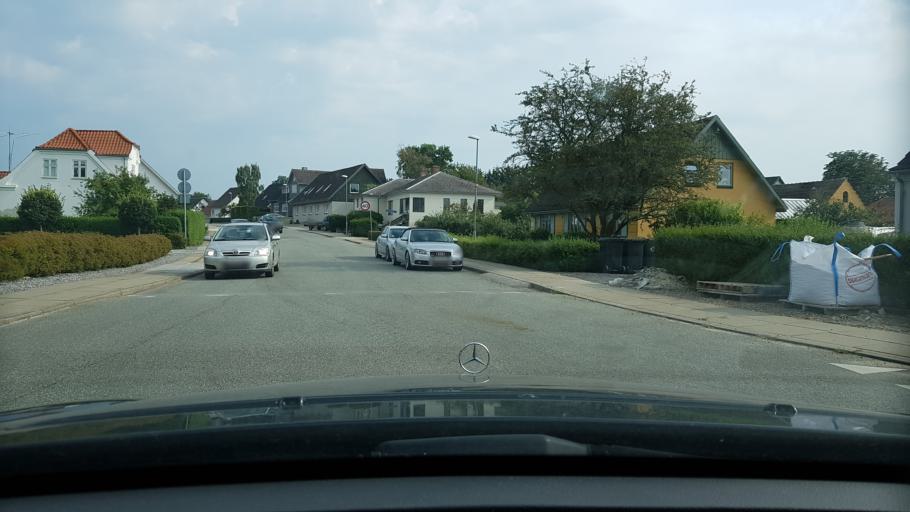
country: DK
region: North Denmark
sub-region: Alborg Kommune
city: Hals
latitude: 56.9699
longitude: 10.2170
